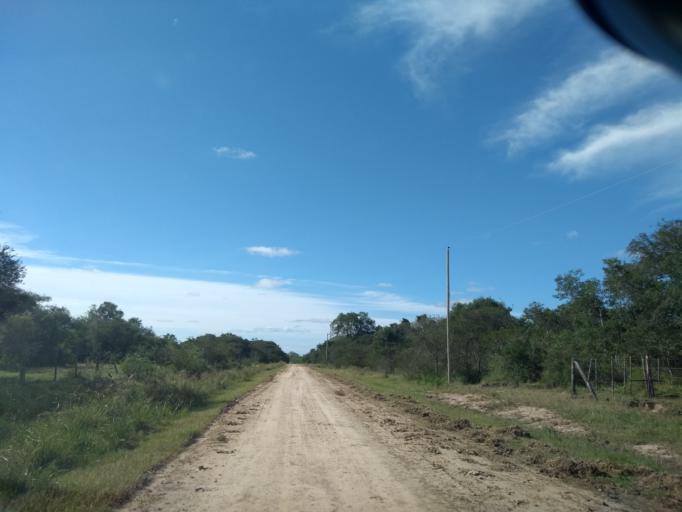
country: AR
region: Chaco
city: Margarita Belen
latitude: -27.2849
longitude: -58.9289
